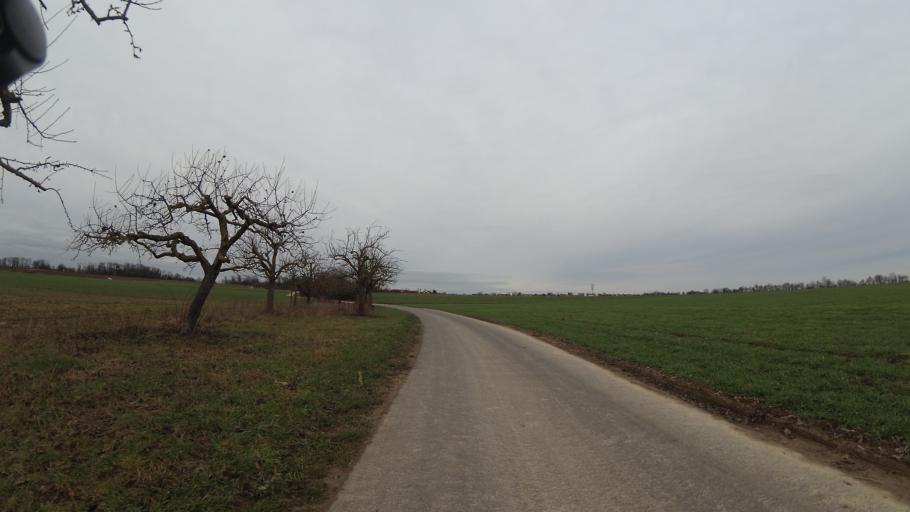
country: DE
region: Baden-Wuerttemberg
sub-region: Regierungsbezirk Stuttgart
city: Oedheim
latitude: 49.2272
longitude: 9.2494
